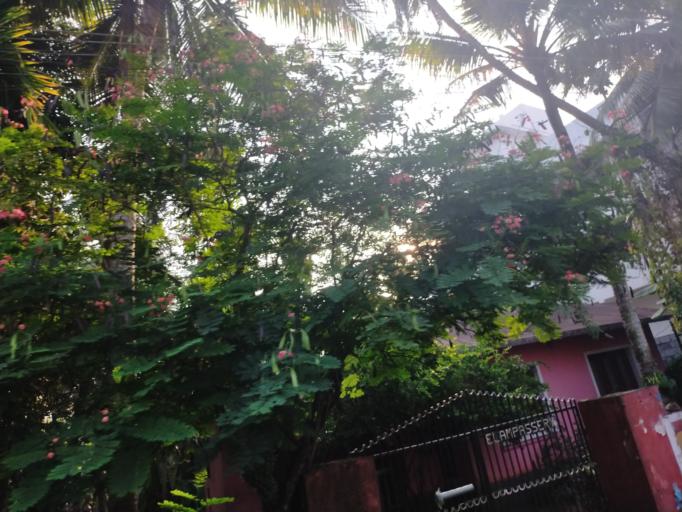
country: IN
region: Kerala
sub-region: Kottayam
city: Vaikam
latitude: 9.7548
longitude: 76.5007
